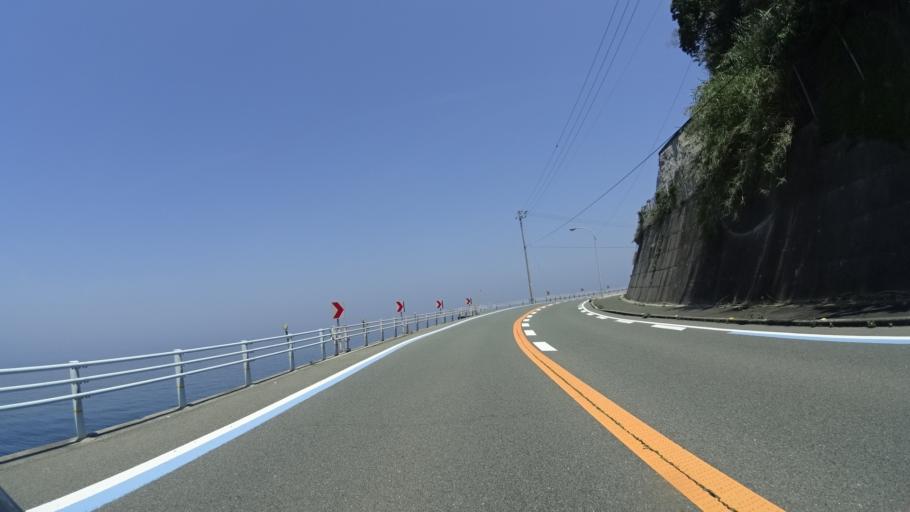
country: JP
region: Ehime
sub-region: Nishiuwa-gun
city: Ikata-cho
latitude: 33.5676
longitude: 132.4335
